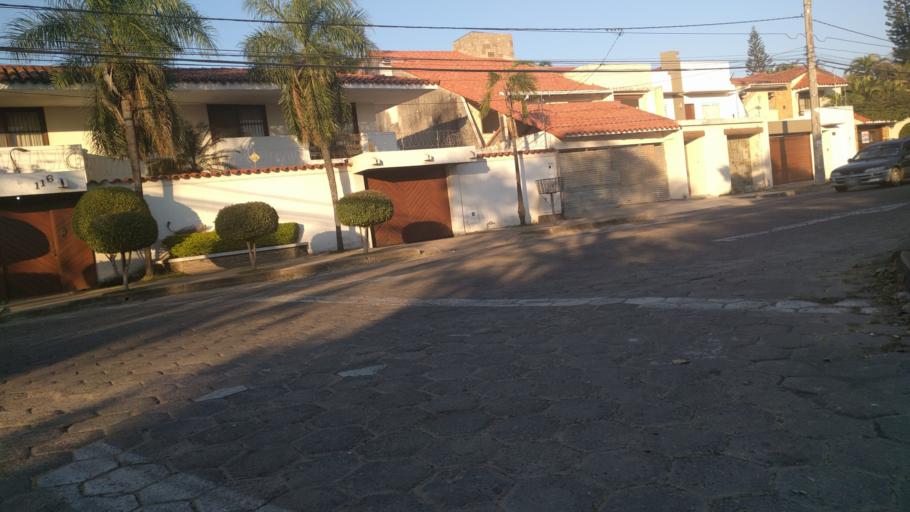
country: BO
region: Santa Cruz
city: Santa Cruz de la Sierra
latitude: -17.7968
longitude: -63.1966
